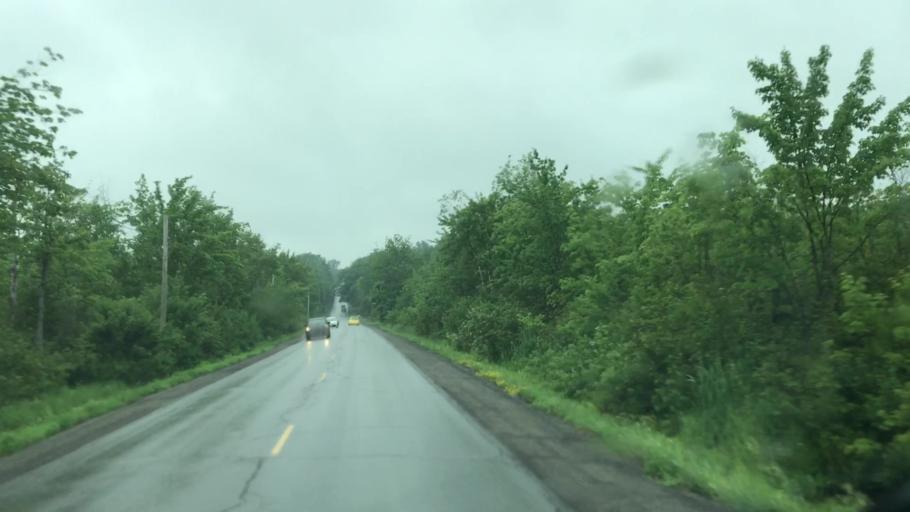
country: US
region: Maine
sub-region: Penobscot County
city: Veazie
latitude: 44.8721
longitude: -68.7146
